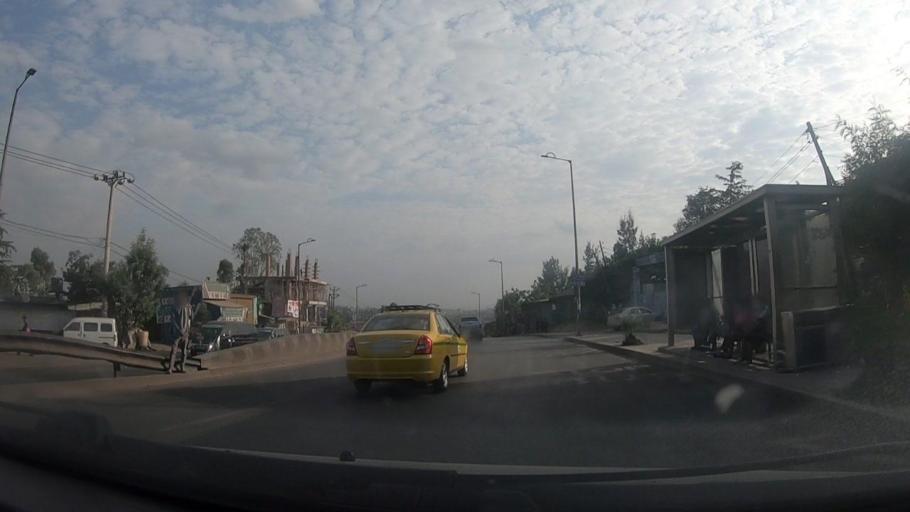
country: ET
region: Adis Abeba
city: Addis Ababa
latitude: 8.9785
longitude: 38.7339
